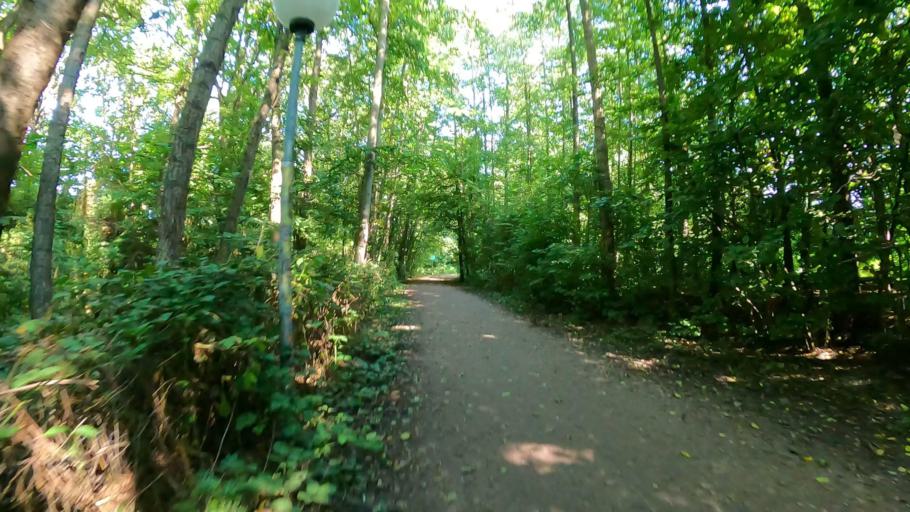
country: DE
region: Schleswig-Holstein
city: Henstedt-Ulzburg
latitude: 53.7840
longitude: 9.9801
